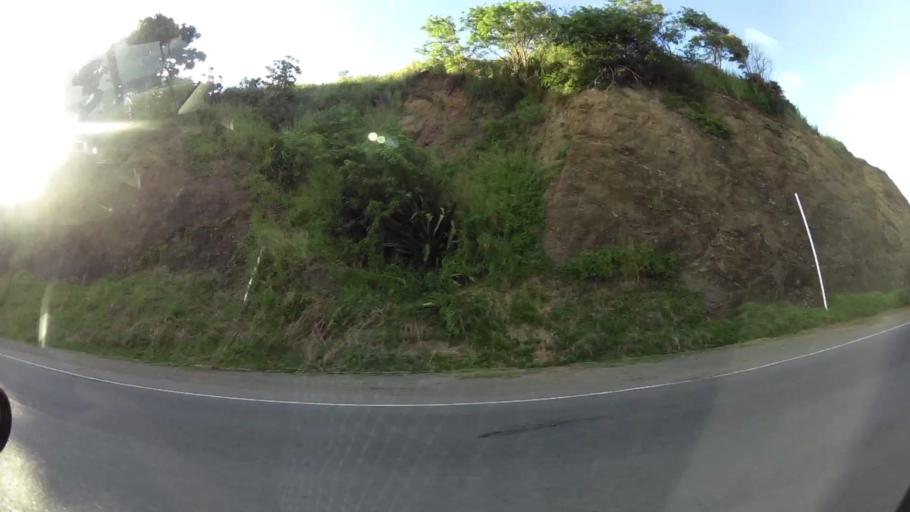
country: TT
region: Tobago
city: Scarborough
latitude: 11.1916
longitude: -60.6945
